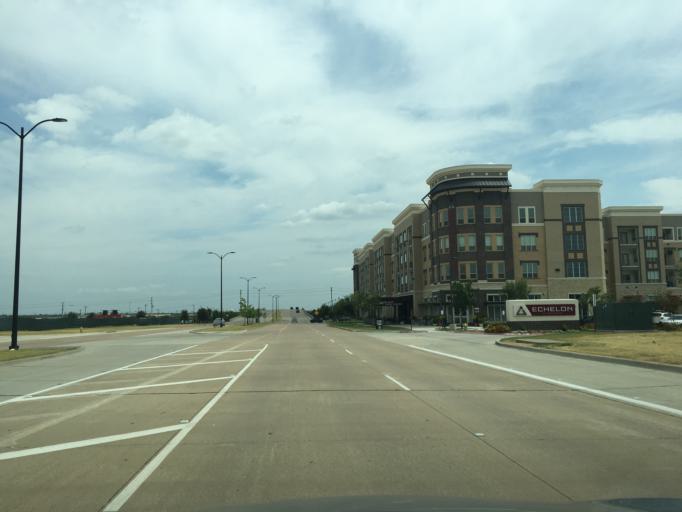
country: US
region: Texas
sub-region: Collin County
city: Frisco
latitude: 33.1038
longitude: -96.7999
